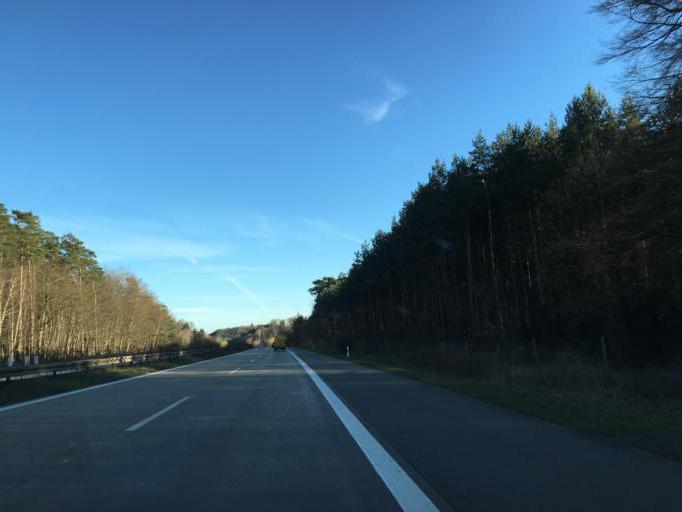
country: DE
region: Mecklenburg-Vorpommern
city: Lalendorf
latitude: 53.7456
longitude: 12.3329
